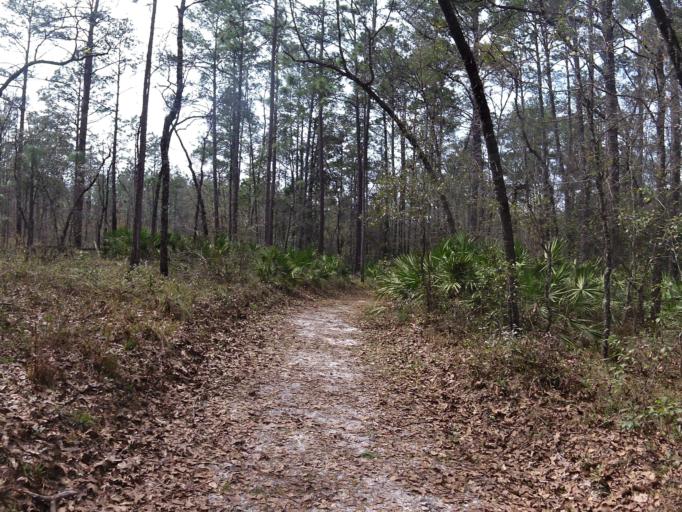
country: US
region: Florida
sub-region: Clay County
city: Middleburg
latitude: 30.1260
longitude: -81.8872
